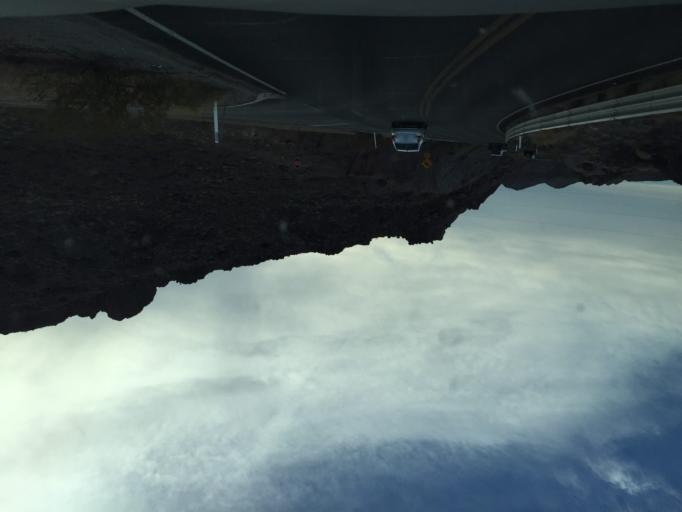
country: US
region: Nevada
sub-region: Clark County
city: Boulder City
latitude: 36.0148
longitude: -114.7597
